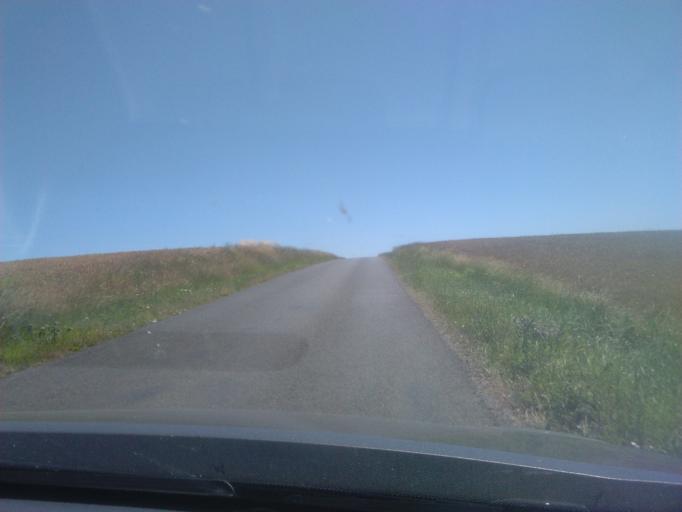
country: FR
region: Centre
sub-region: Departement du Loir-et-Cher
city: Herbault
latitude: 47.6408
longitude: 1.1969
